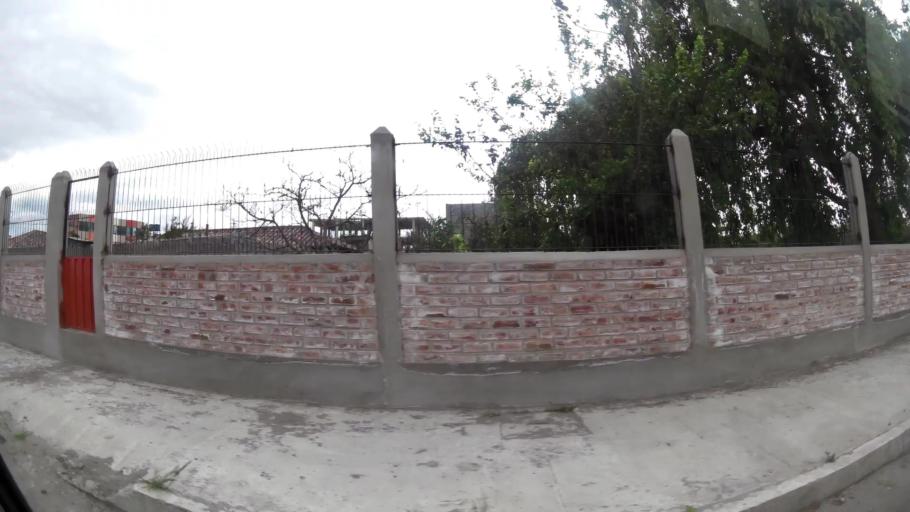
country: EC
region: Tungurahua
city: Ambato
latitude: -1.2803
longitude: -78.6221
